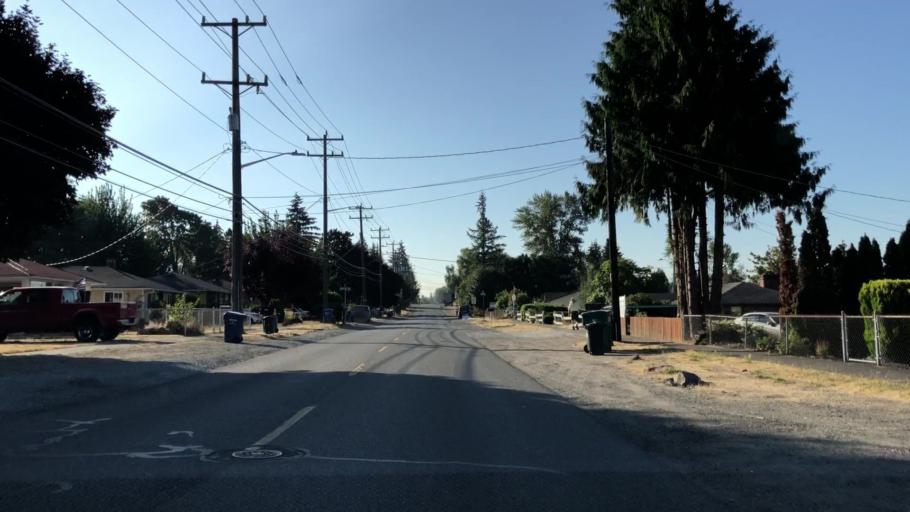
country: US
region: Washington
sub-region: King County
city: Tukwila
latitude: 47.5010
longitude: -122.2686
